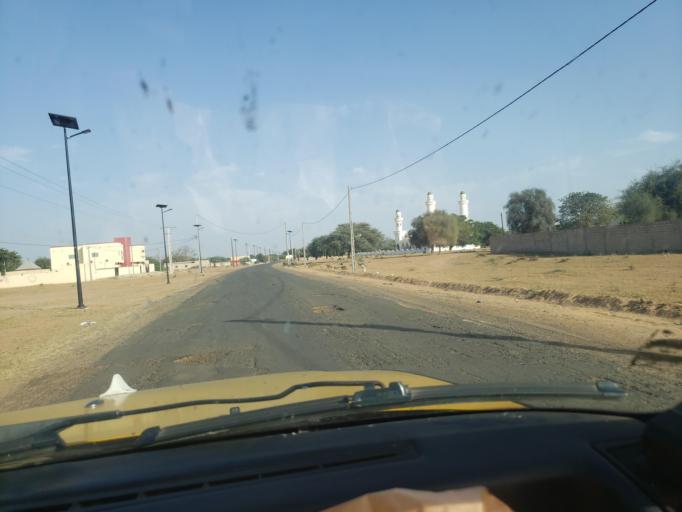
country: SN
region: Louga
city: Louga
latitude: 15.5127
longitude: -15.9950
